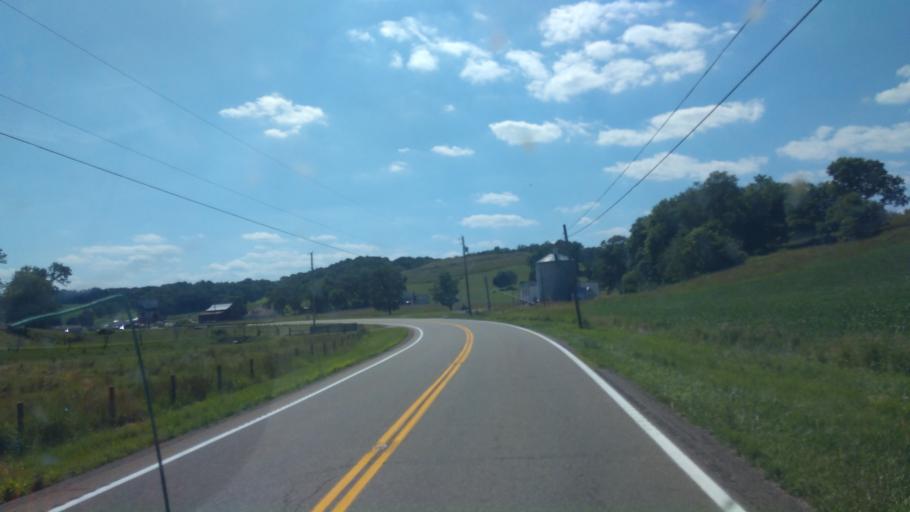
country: US
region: Ohio
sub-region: Carroll County
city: Carrollton
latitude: 40.5756
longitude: -81.1183
